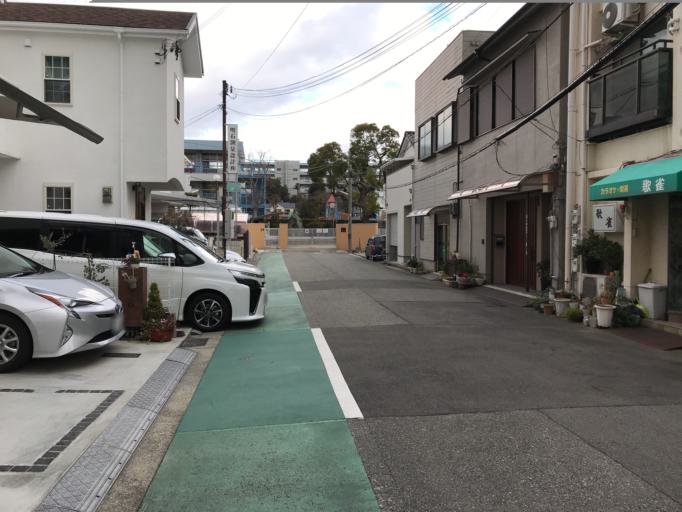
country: JP
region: Hyogo
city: Akashi
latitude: 34.6487
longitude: 134.9980
